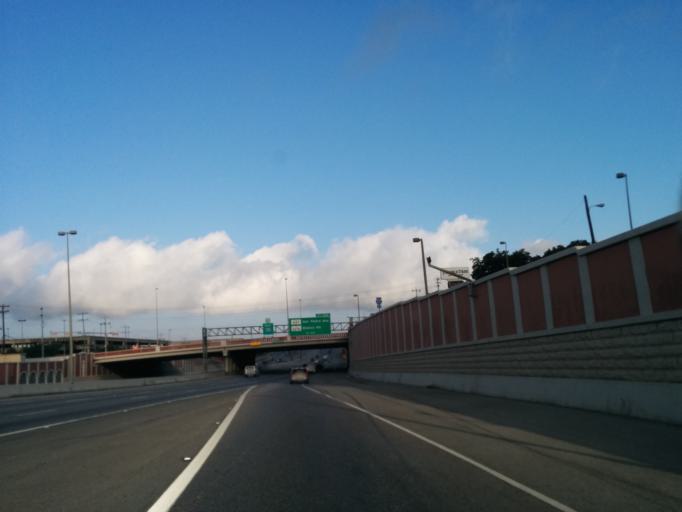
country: US
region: Texas
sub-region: Bexar County
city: Castle Hills
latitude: 29.5207
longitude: -98.4901
